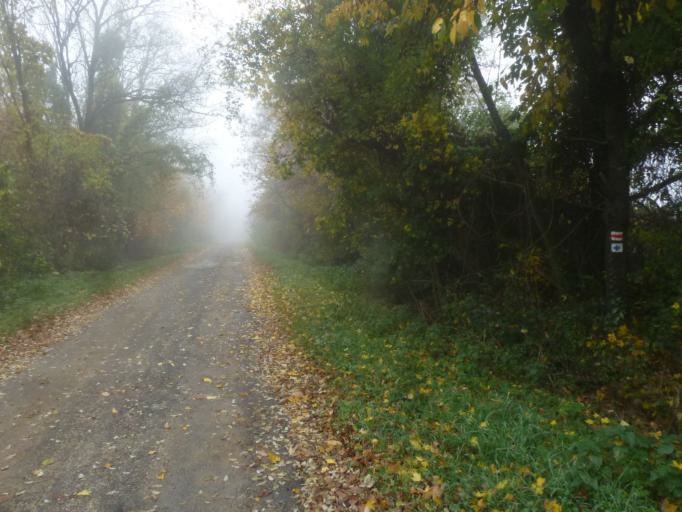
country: HU
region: Zala
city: Nagykanizsa
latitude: 46.5614
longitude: 17.0201
